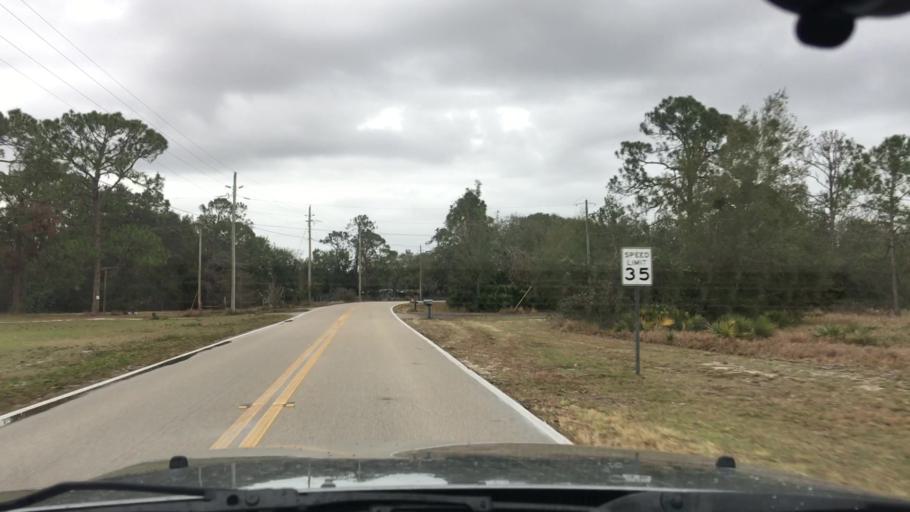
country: US
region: Florida
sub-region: Highlands County
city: Sebring
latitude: 27.4372
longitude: -81.4444
